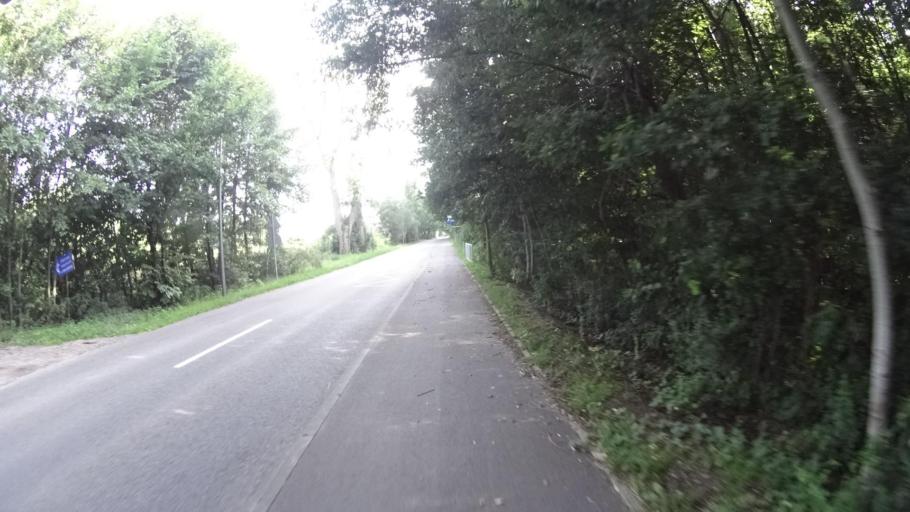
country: PL
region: Masovian Voivodeship
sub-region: Powiat pruszkowski
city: Nadarzyn
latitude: 52.0374
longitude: 20.7823
